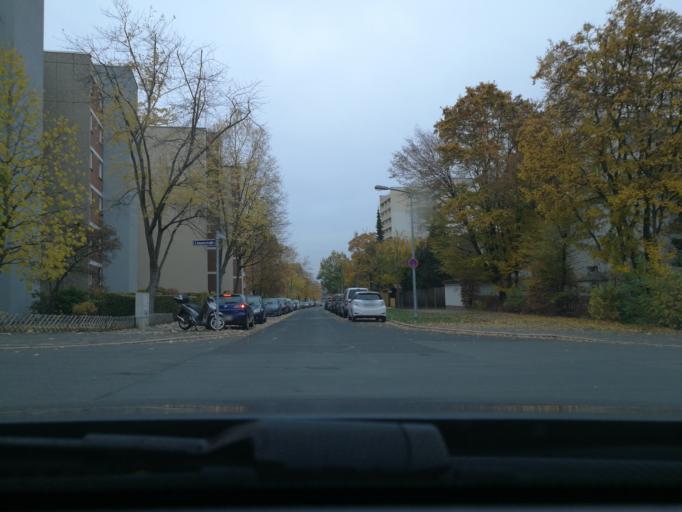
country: DE
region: Bavaria
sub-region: Regierungsbezirk Mittelfranken
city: Nuernberg
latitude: 49.4662
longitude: 11.1054
